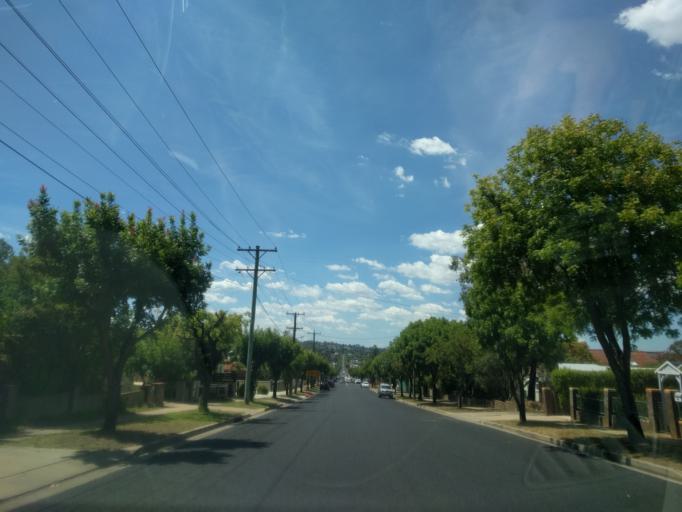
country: AU
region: New South Wales
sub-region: Armidale Dumaresq
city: Armidale
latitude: -30.5190
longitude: 151.6672
